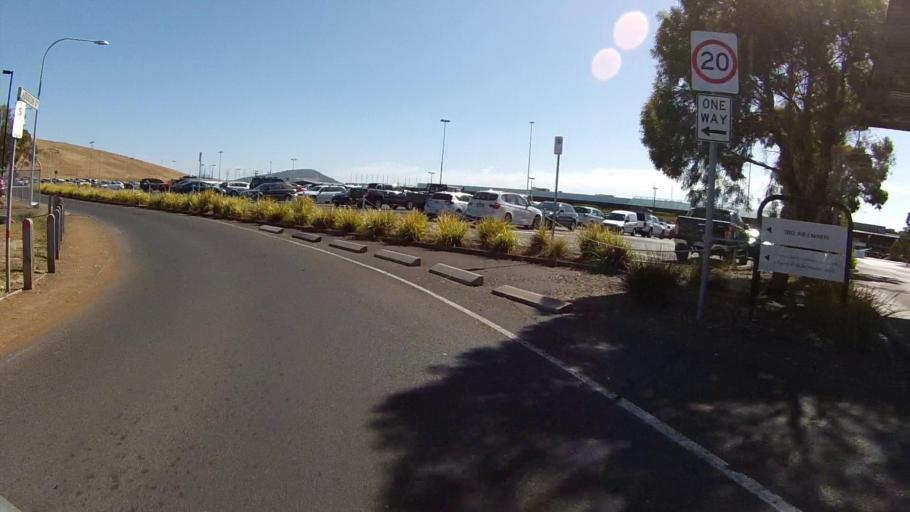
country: AU
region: Tasmania
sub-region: Clarence
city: Seven Mile Beach
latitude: -42.8378
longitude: 147.5040
